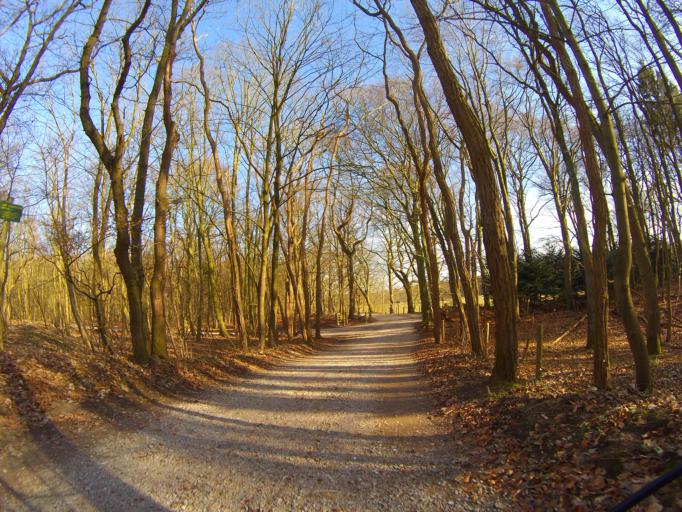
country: NL
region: North Holland
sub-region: Gemeente Naarden
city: Naarden
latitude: 52.3052
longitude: 5.2015
